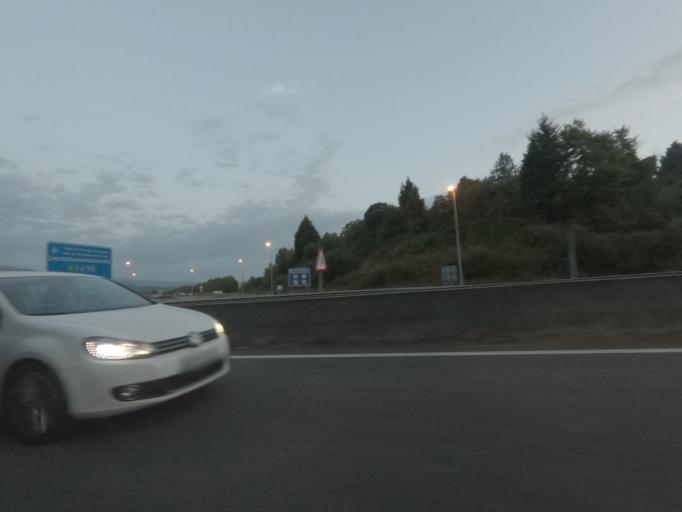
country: ES
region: Galicia
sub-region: Provincia de Pontevedra
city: Tui
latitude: 42.0678
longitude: -8.6414
